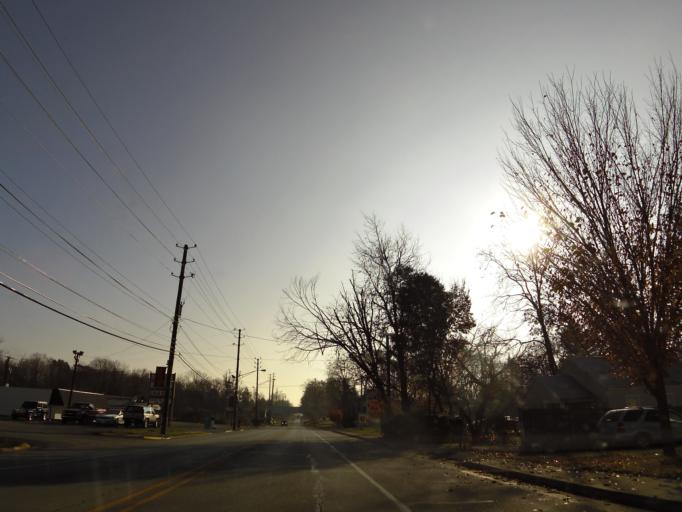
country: US
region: Indiana
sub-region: Marion County
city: Clermont
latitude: 39.8143
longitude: -86.3183
